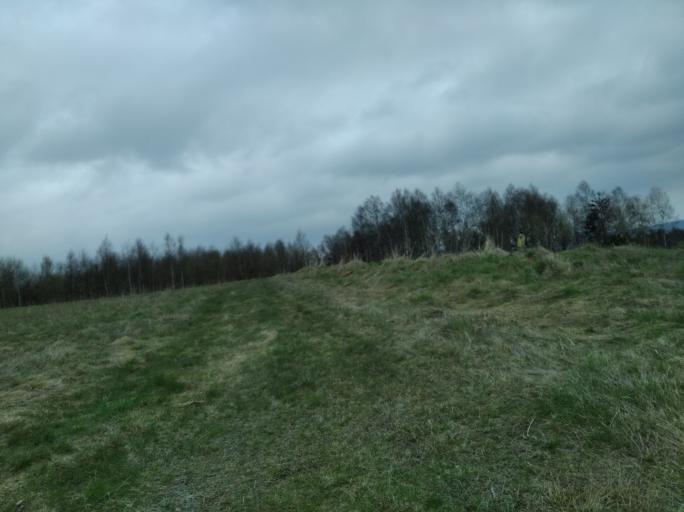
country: PL
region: Subcarpathian Voivodeship
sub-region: Powiat strzyzowski
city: Jawornik
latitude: 49.8200
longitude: 21.9007
